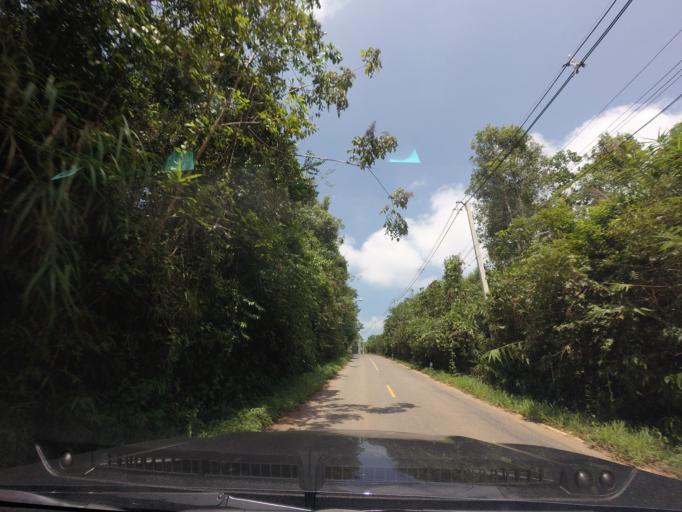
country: TH
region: Loei
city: Na Haeo
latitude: 17.4691
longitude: 100.9222
